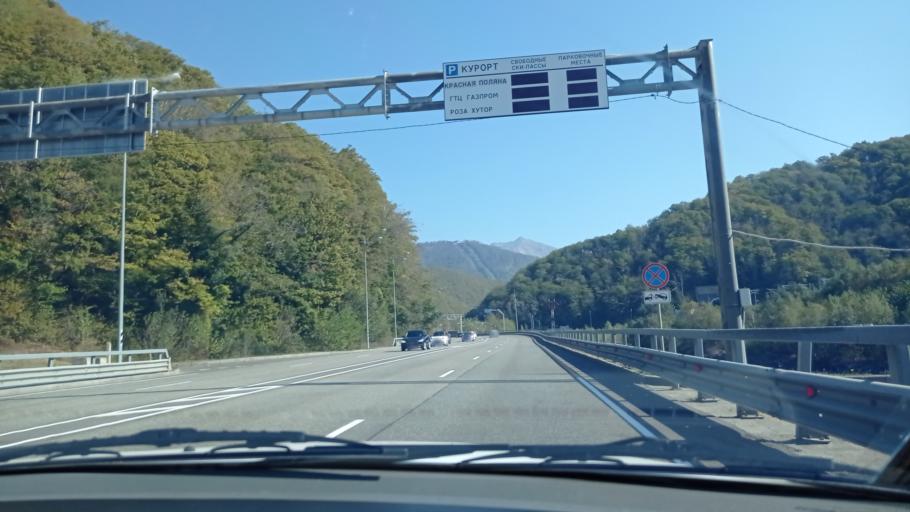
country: RU
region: Krasnodarskiy
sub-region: Sochi City
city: Krasnaya Polyana
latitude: 43.6852
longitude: 40.2403
